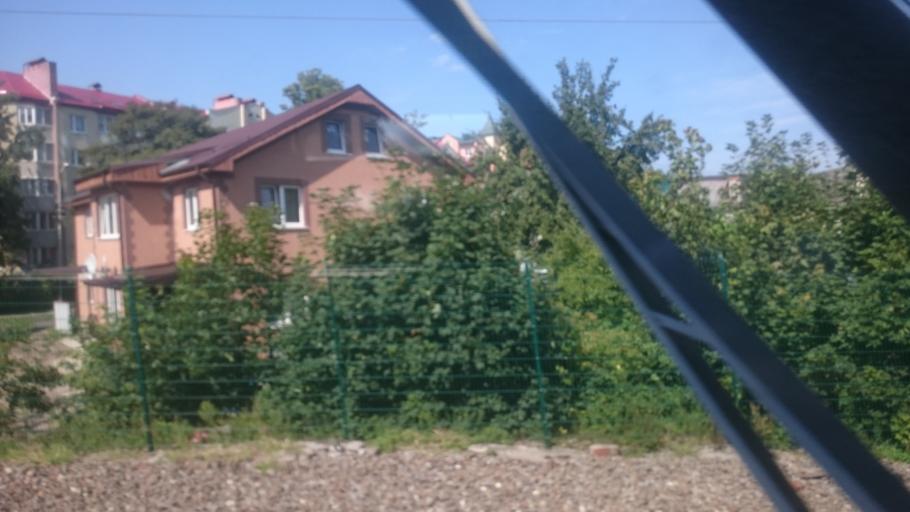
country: RU
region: Kaliningrad
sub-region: Gorod Kaliningrad
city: Kaliningrad
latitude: 54.7435
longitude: 20.5288
